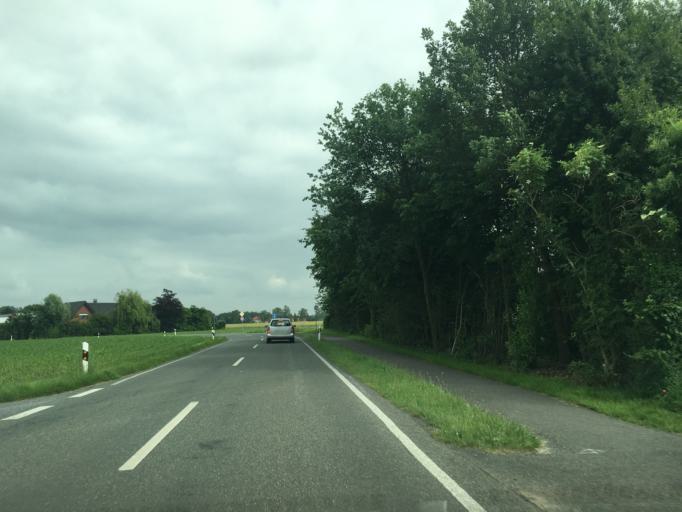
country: DE
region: North Rhine-Westphalia
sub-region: Regierungsbezirk Munster
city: Horstmar
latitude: 52.1066
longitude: 7.3035
